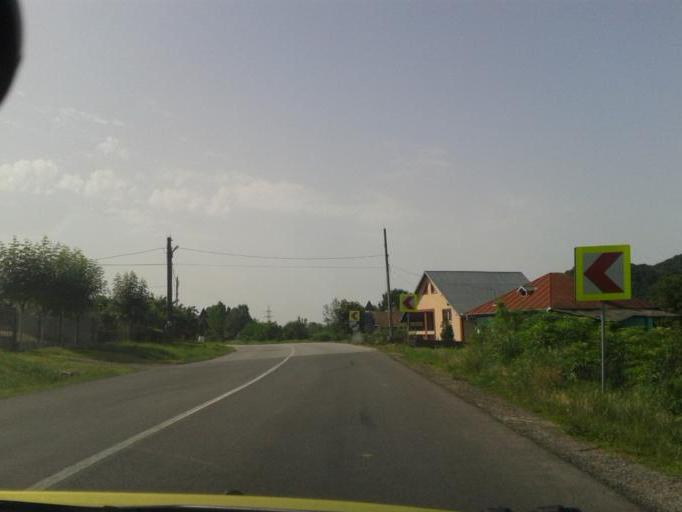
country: RO
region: Valcea
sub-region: Comuna Mihaesti
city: Mihaesti
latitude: 45.0503
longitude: 24.2511
